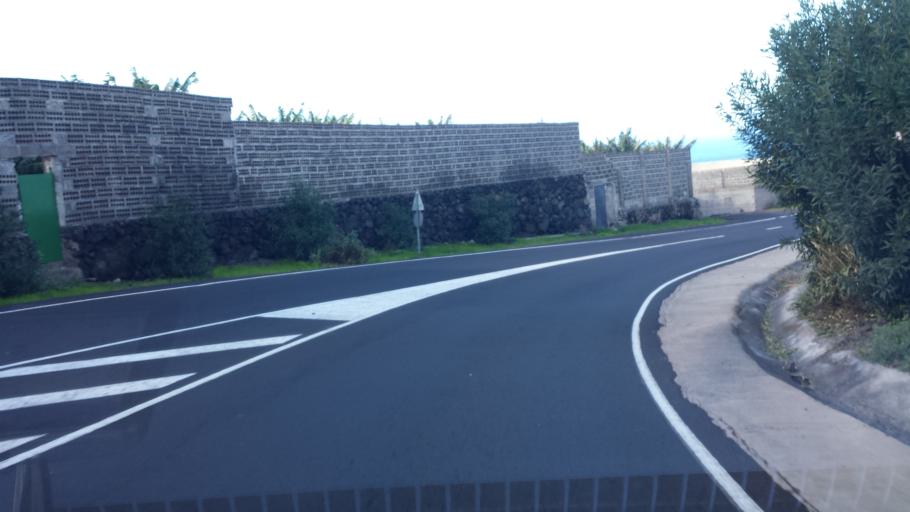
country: ES
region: Canary Islands
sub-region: Provincia de Santa Cruz de Tenerife
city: Tazacorte
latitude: 28.5977
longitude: -17.9102
